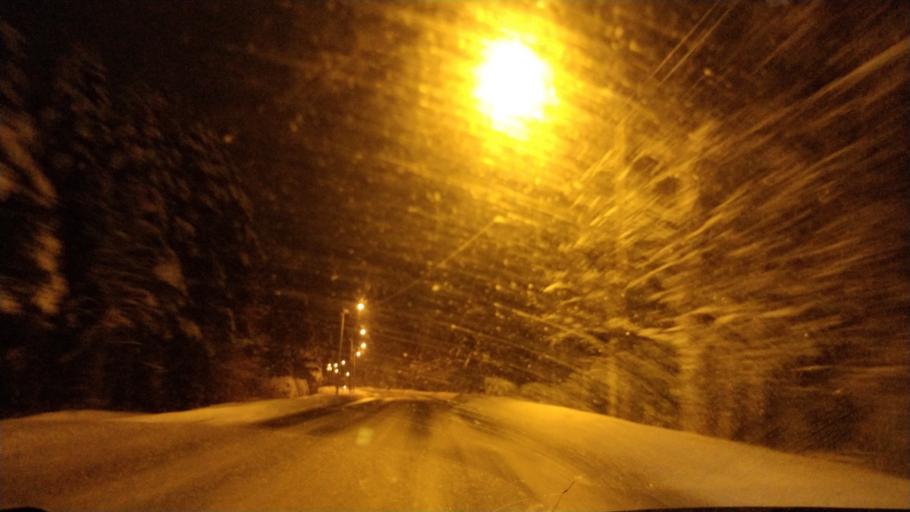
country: FI
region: Lapland
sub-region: Rovaniemi
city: Rovaniemi
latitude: 66.3804
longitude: 25.3794
